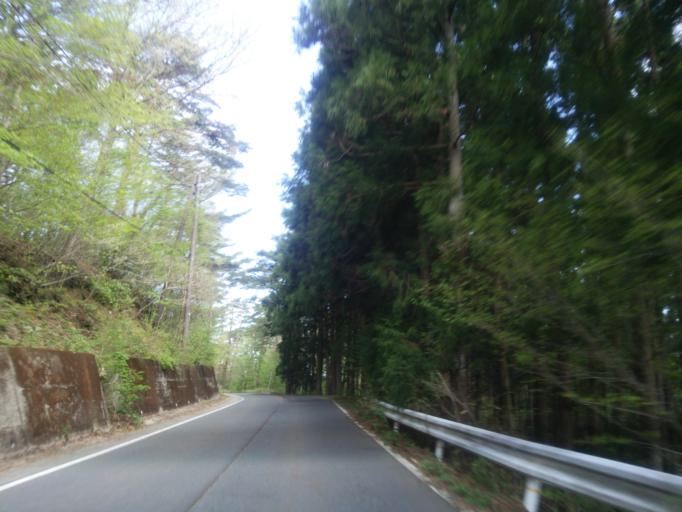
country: JP
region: Fukushima
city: Nihommatsu
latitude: 37.6100
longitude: 140.3526
